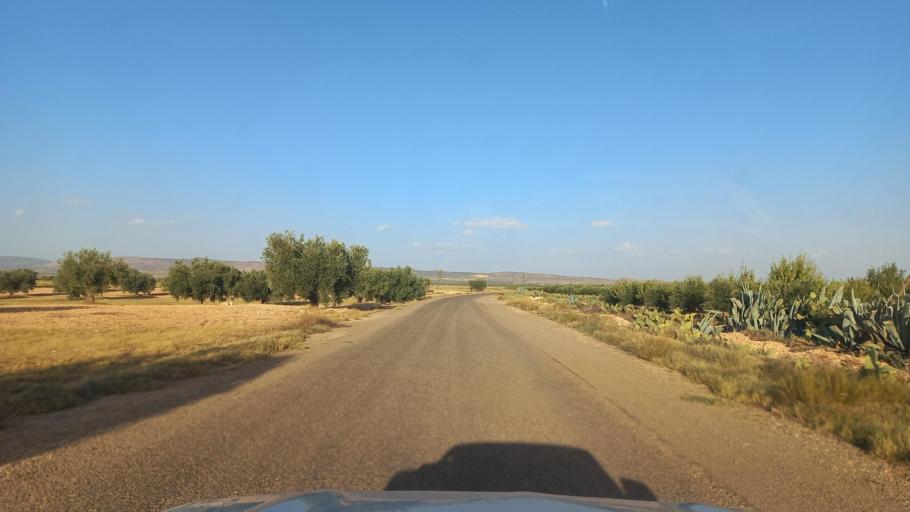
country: TN
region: Al Qasrayn
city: Kasserine
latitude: 35.2871
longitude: 9.0364
